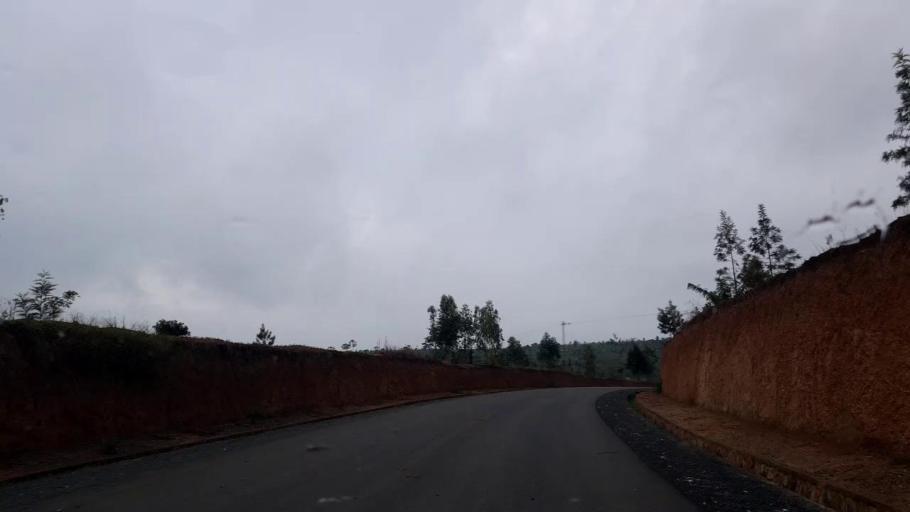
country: RW
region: Northern Province
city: Byumba
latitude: -1.4238
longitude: 30.2705
